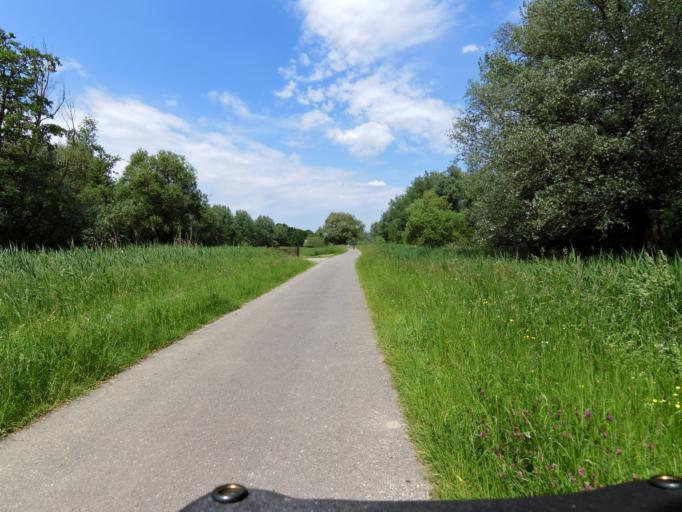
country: NL
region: North Brabant
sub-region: Gemeente Woudrichem
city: Woudrichem
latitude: 51.8074
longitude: 5.0606
